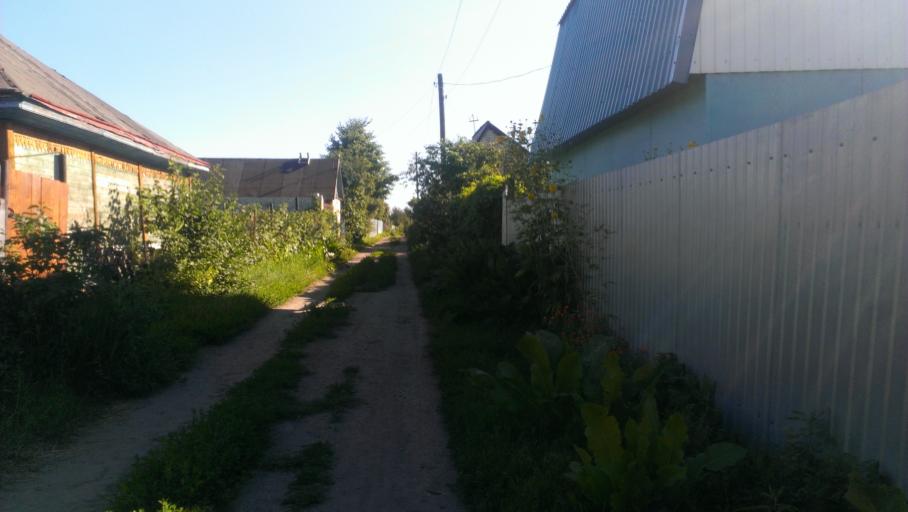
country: RU
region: Altai Krai
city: Novosilikatnyy
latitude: 53.3250
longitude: 83.6698
